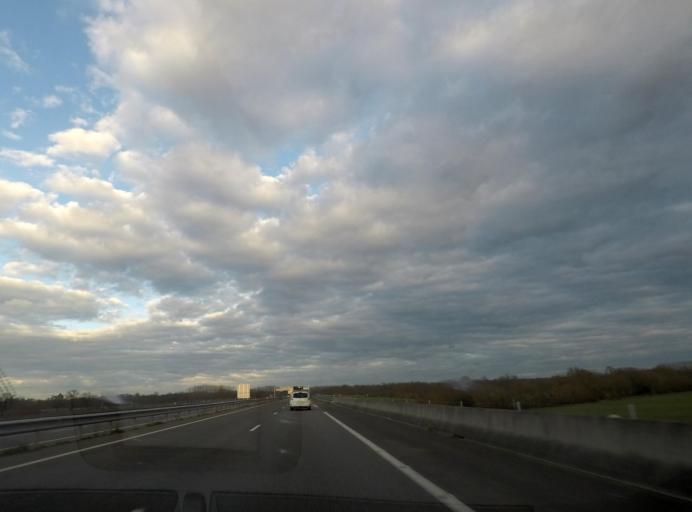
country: FR
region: Rhone-Alpes
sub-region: Departement de l'Ain
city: Grieges
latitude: 46.2734
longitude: 4.8450
